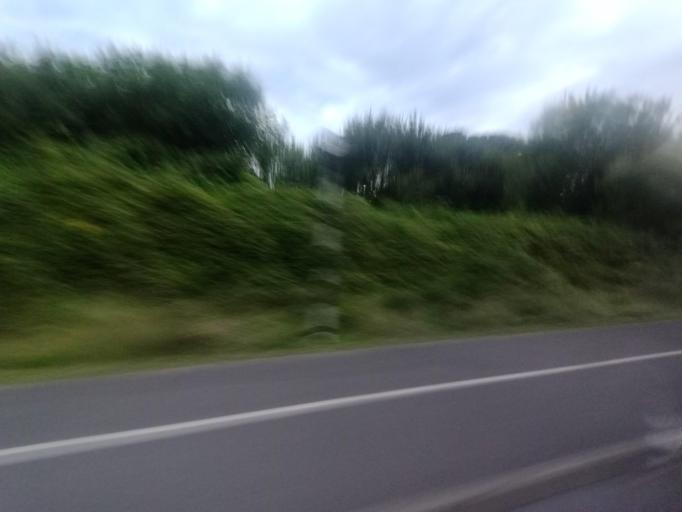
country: IE
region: Leinster
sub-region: Laois
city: Portlaoise
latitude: 53.0384
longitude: -7.3176
